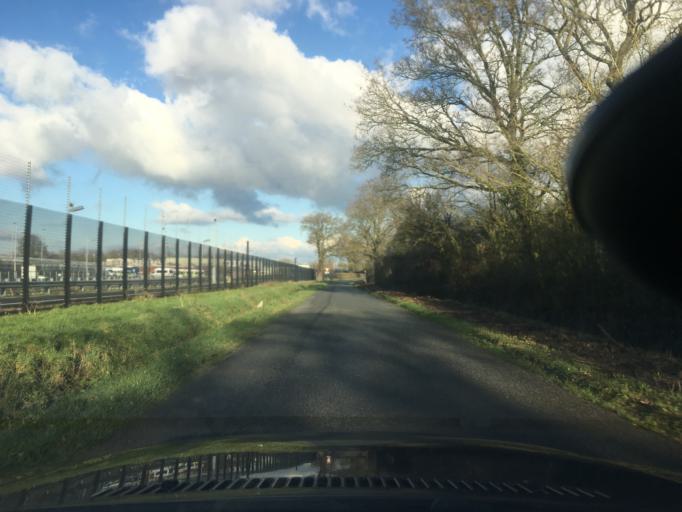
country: GB
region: England
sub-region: West Berkshire
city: Stratfield Mortimer
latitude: 51.4056
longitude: -1.0182
